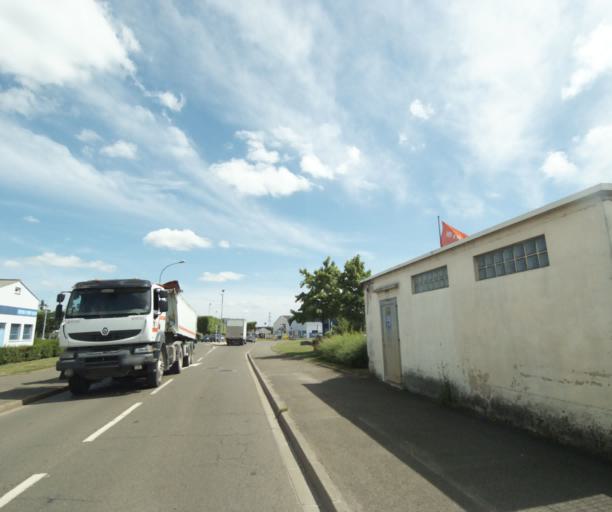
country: FR
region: Centre
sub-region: Departement d'Eure-et-Loir
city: Luce
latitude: 48.4314
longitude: 1.4631
